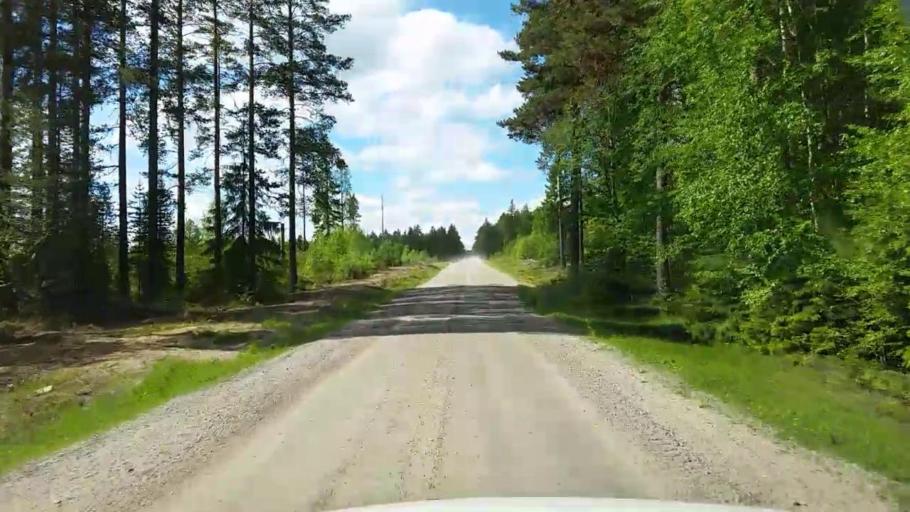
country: SE
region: Gaevleborg
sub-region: Ovanakers Kommun
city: Edsbyn
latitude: 61.5728
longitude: 15.9174
